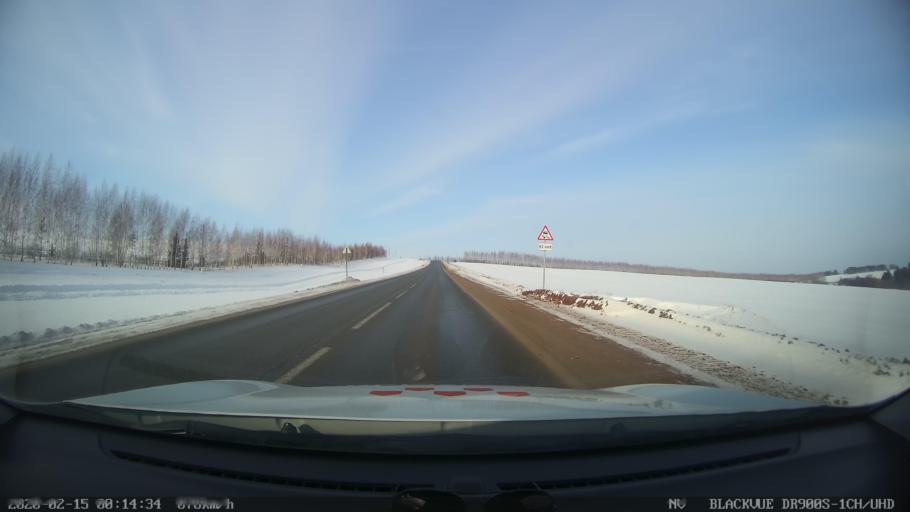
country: RU
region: Tatarstan
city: Stolbishchi
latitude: 55.4874
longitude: 49.0044
